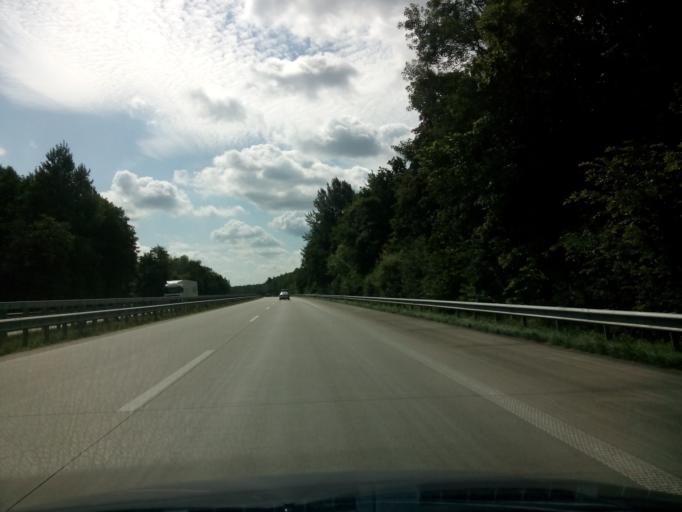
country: DE
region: Lower Saxony
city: Lemwerder
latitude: 53.2119
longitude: 8.6561
